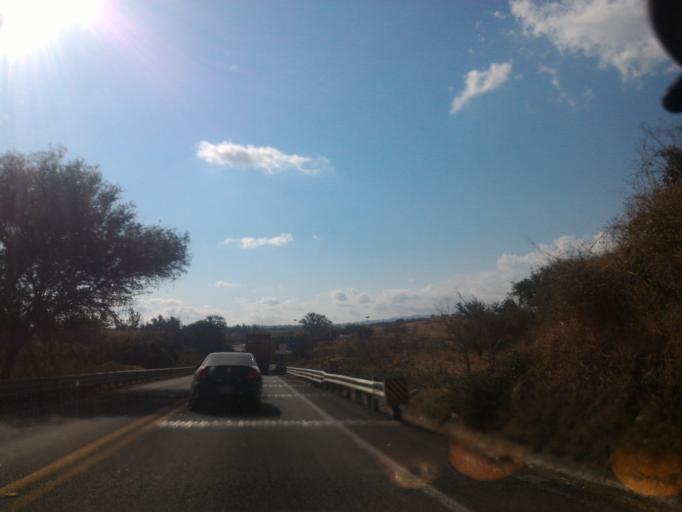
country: MX
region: Jalisco
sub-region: Tonila
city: San Marcos
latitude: 19.4342
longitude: -103.4909
